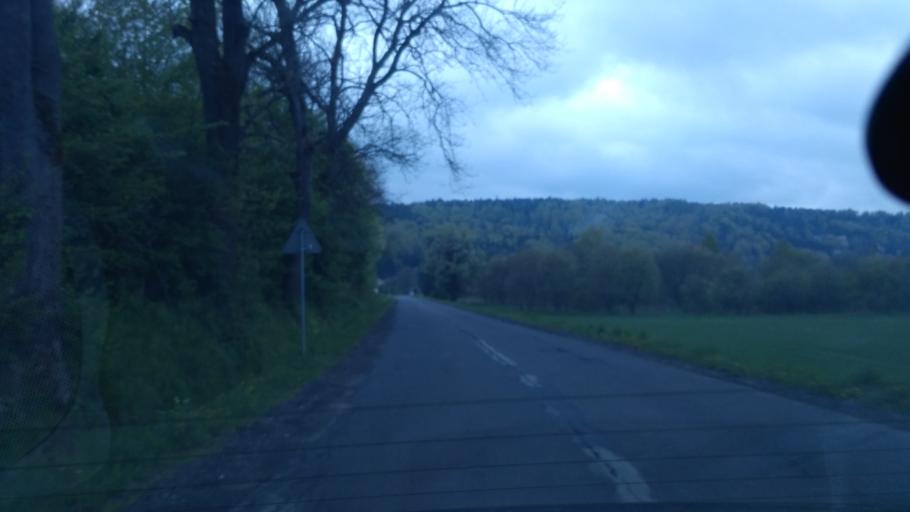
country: PL
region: Subcarpathian Voivodeship
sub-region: Powiat brzozowski
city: Nozdrzec
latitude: 49.7307
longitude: 22.2166
